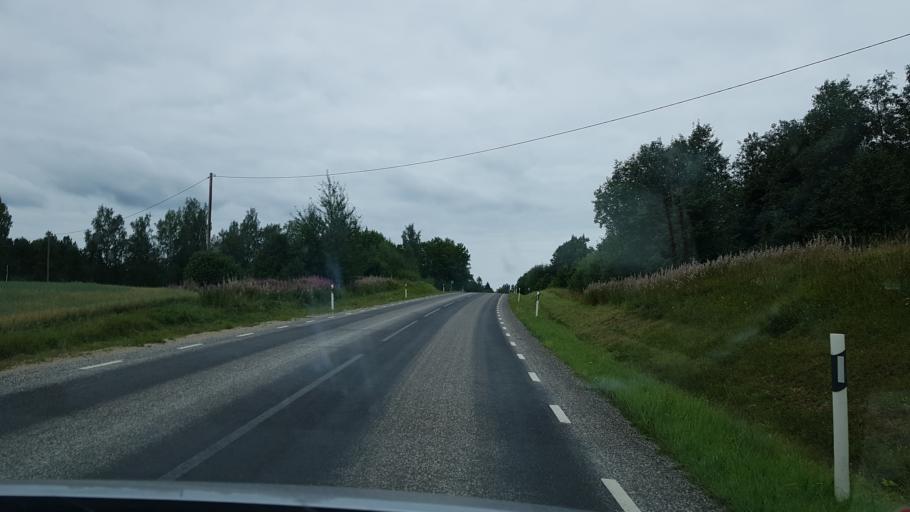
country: EE
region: Vorumaa
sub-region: Antsla vald
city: Vana-Antsla
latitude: 58.0101
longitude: 26.5987
